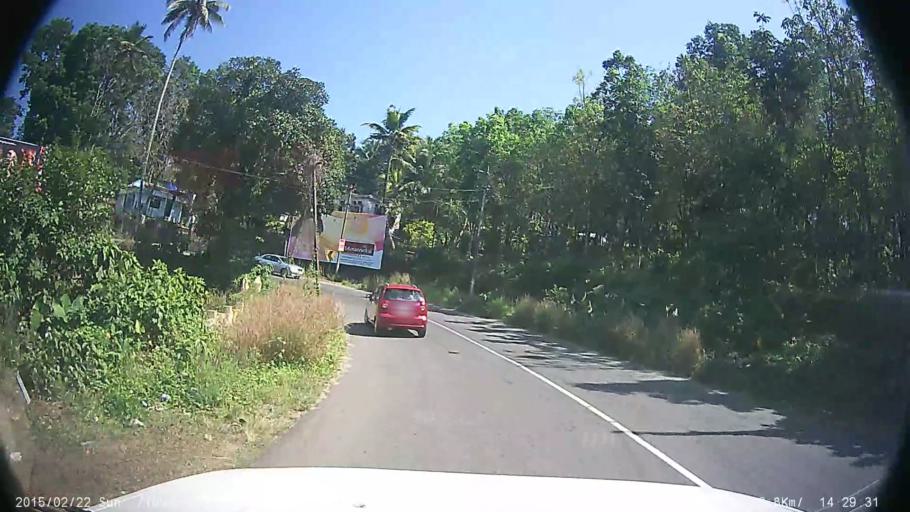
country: IN
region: Kerala
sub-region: Kottayam
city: Erattupetta
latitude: 9.5654
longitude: 76.7433
